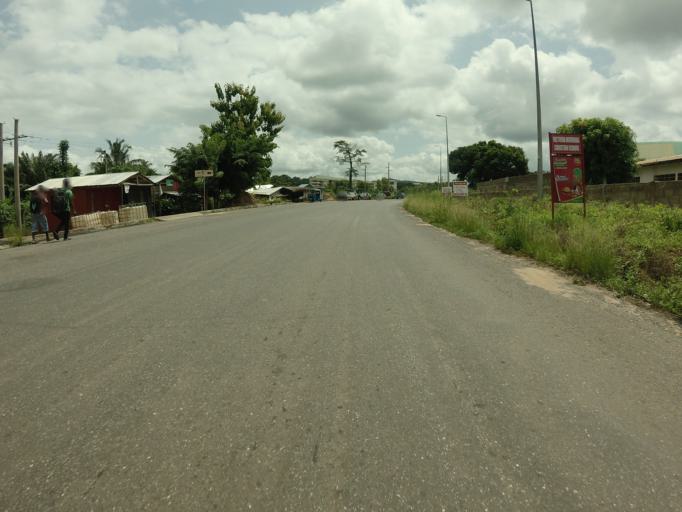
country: GH
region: Volta
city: Ho
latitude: 6.5898
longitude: 0.4736
